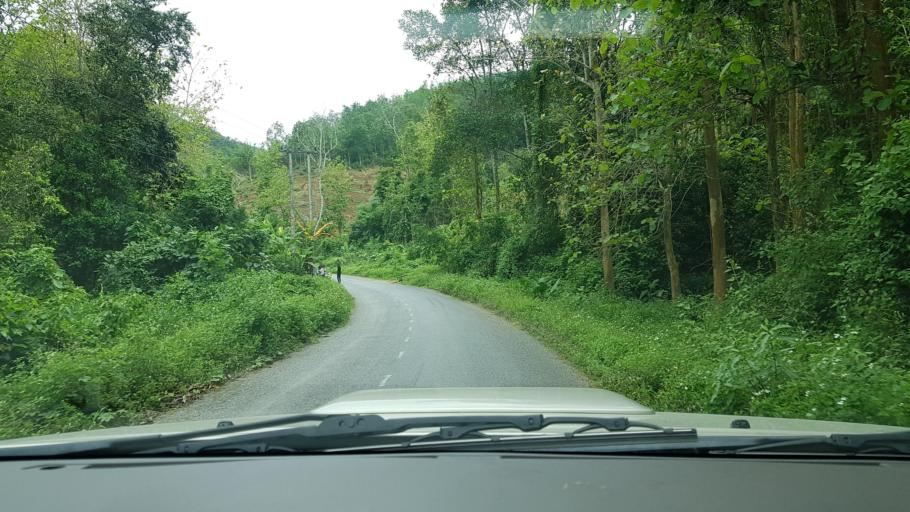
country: LA
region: Phongsali
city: Khoa
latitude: 21.0598
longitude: 102.3876
